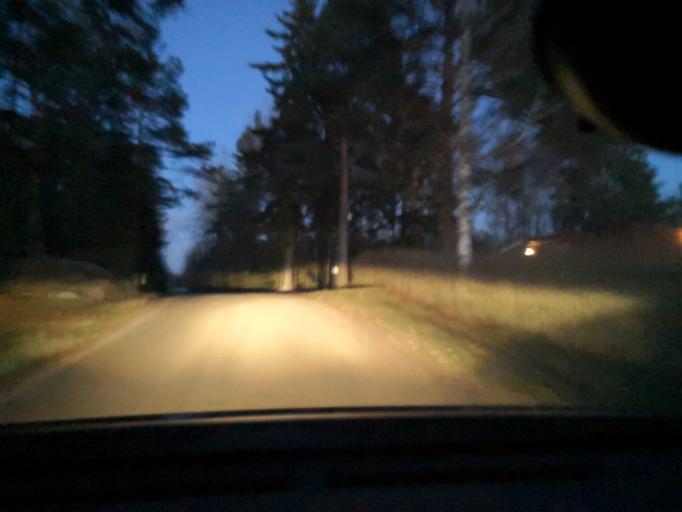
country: SE
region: Vaestmanland
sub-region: Sala Kommun
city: Sala
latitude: 59.8765
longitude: 16.7289
